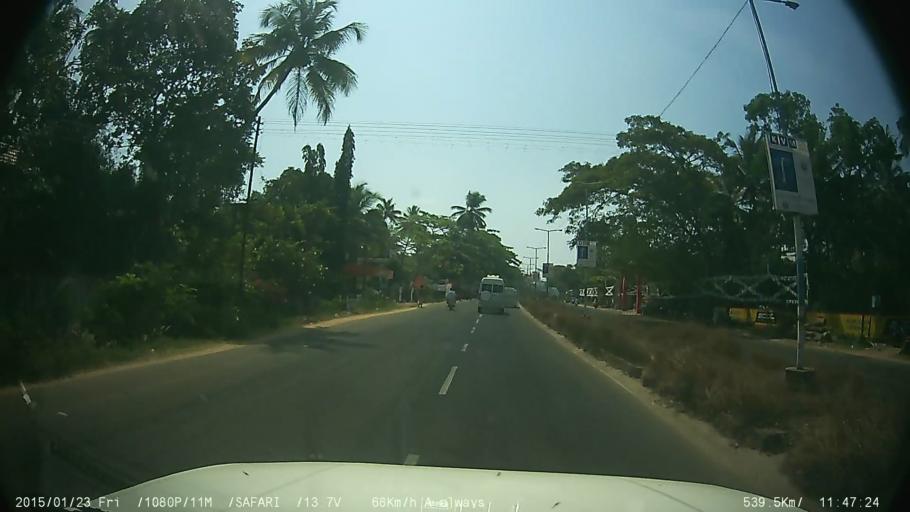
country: IN
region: Kerala
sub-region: Alappuzha
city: Vayalar
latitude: 9.7300
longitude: 76.3189
